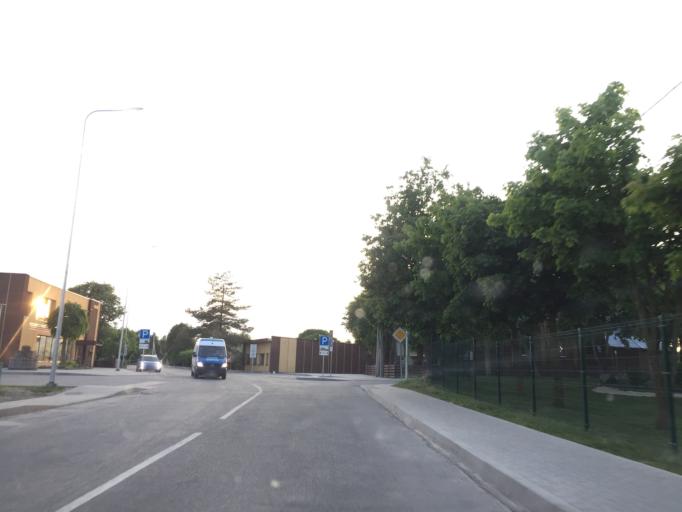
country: LT
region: Siauliu apskritis
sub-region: Siauliai
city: Siauliai
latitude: 55.9832
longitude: 23.1375
